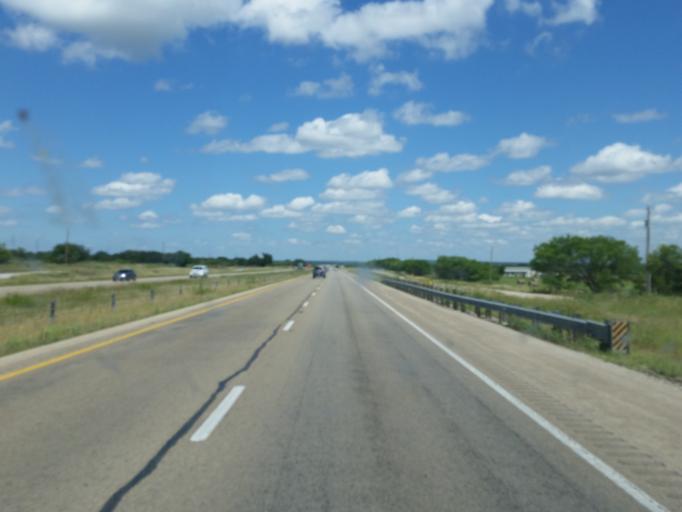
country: US
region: Texas
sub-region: Callahan County
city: Baird
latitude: 32.3897
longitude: -99.3309
